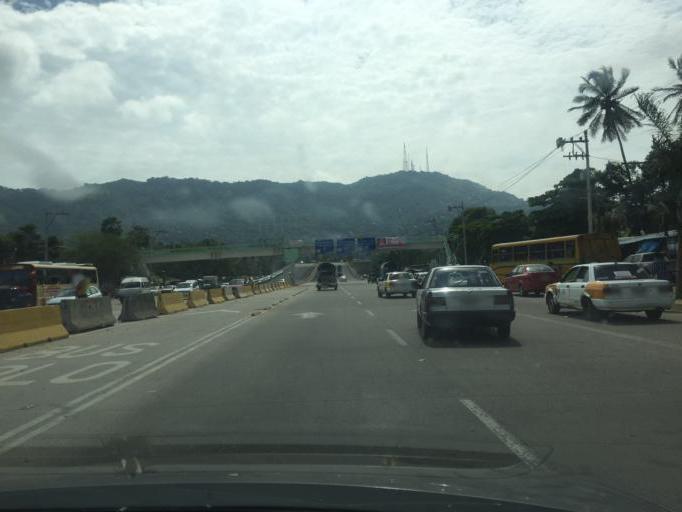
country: MX
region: Guerrero
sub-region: Acapulco de Juarez
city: Colonia Alborada
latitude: 16.8903
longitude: -99.8360
